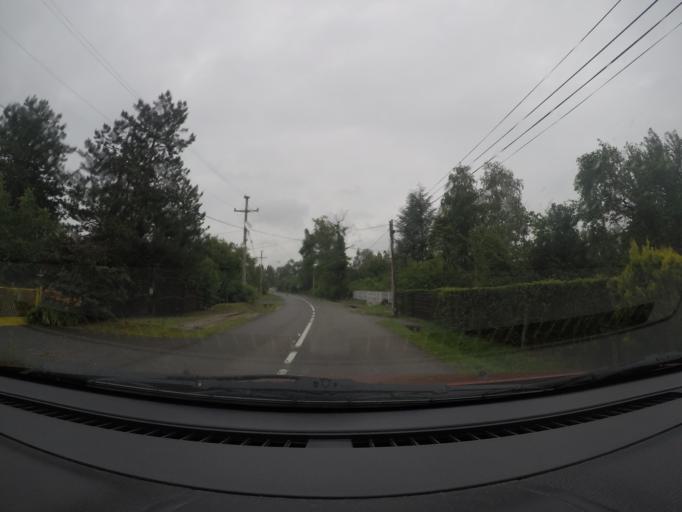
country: RS
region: Central Serbia
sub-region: Belgrade
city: Sopot
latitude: 44.5477
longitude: 20.5377
